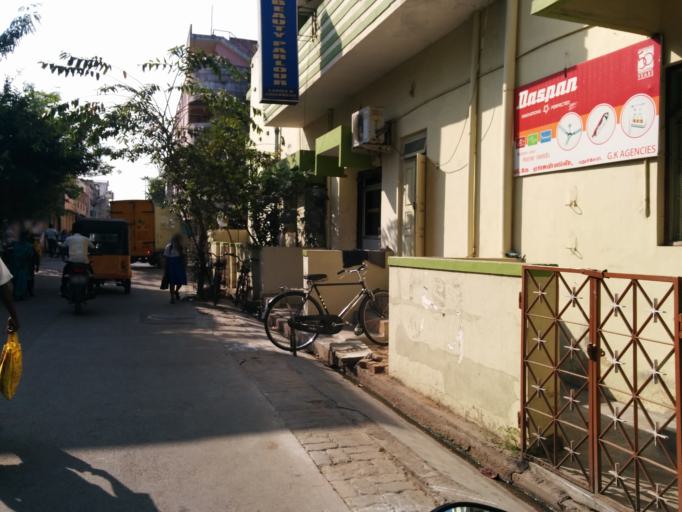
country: IN
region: Pondicherry
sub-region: Puducherry
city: Puducherry
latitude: 11.9511
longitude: 79.8336
